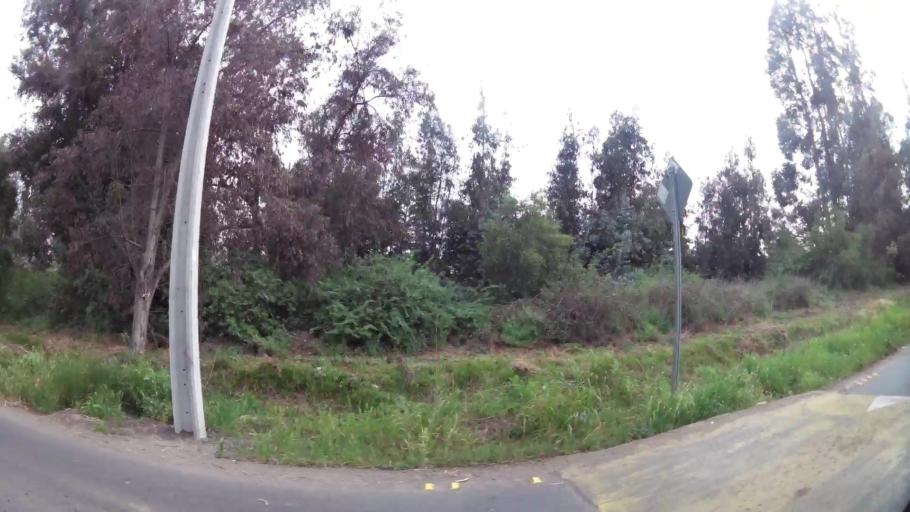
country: CL
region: Santiago Metropolitan
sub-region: Provincia de Chacabuco
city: Chicureo Abajo
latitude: -33.2720
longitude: -70.7051
